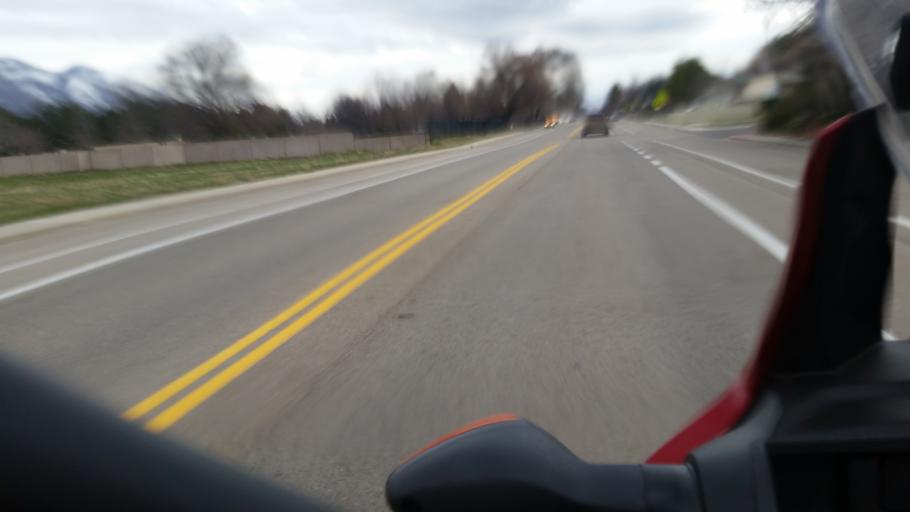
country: US
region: Utah
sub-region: Utah County
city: Orem
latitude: 40.3168
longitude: -111.6863
